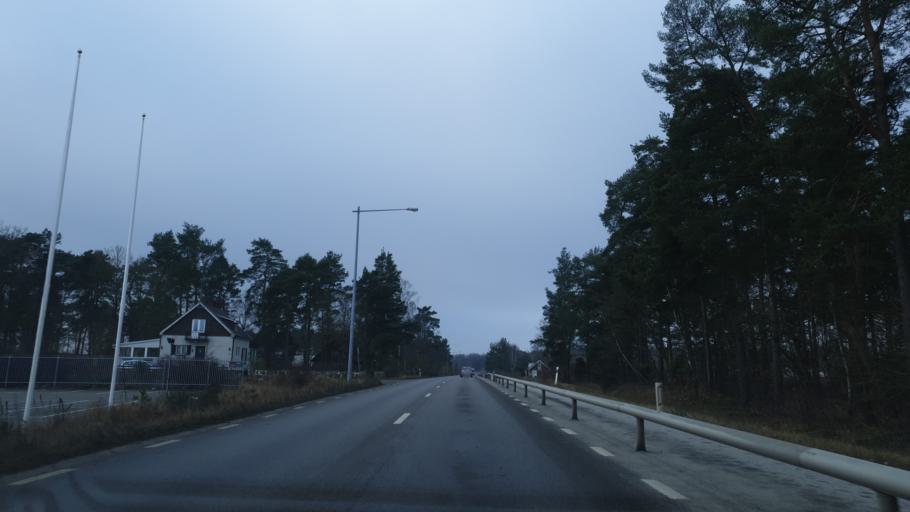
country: SE
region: Blekinge
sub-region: Solvesborgs Kommun
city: Soelvesborg
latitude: 56.1003
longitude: 14.6651
